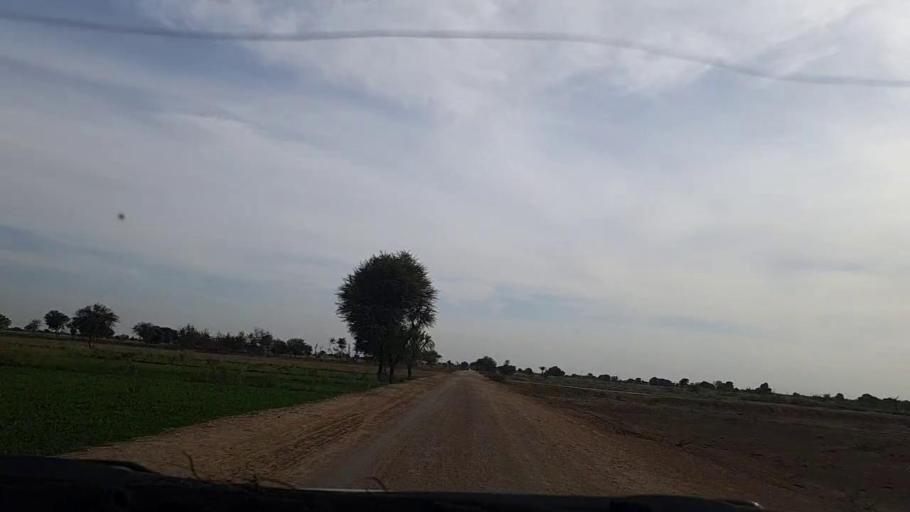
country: PK
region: Sindh
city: Dhoro Naro
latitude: 25.4098
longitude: 69.5182
